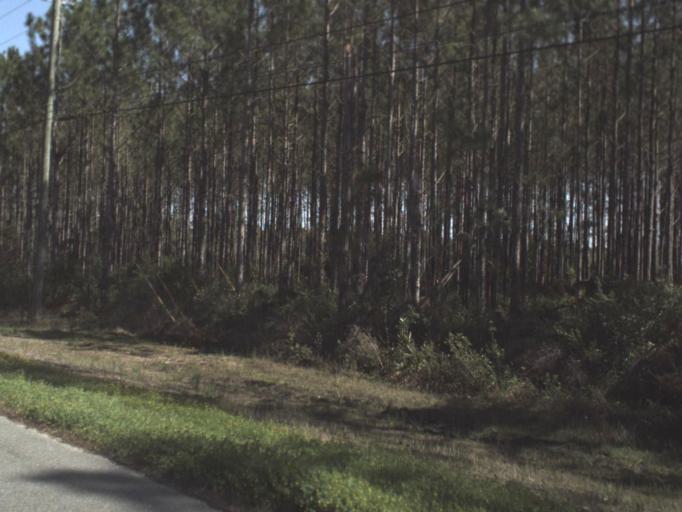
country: US
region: Florida
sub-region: Bay County
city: Lynn Haven
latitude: 30.3224
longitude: -85.6900
